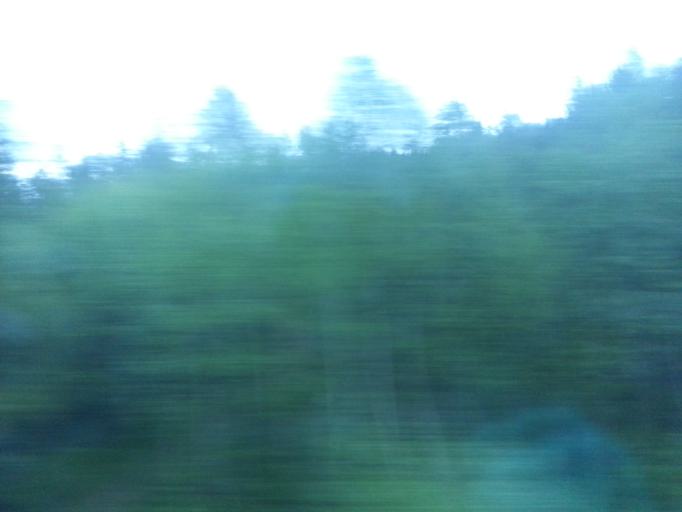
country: NO
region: Oppland
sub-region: Dovre
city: Dombas
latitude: 62.0866
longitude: 9.1437
